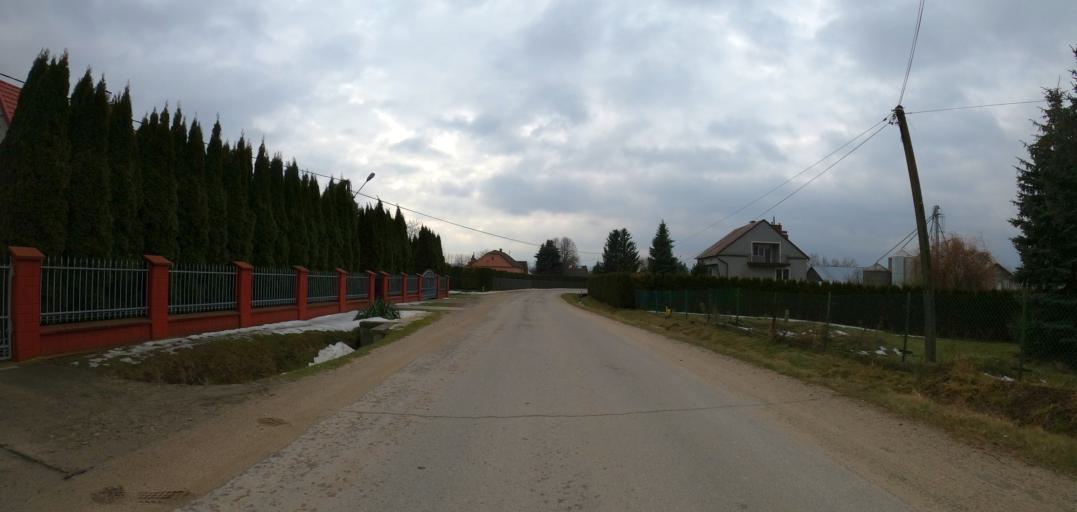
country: PL
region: Subcarpathian Voivodeship
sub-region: Powiat debicki
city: Pilzno
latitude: 49.9789
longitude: 21.3302
